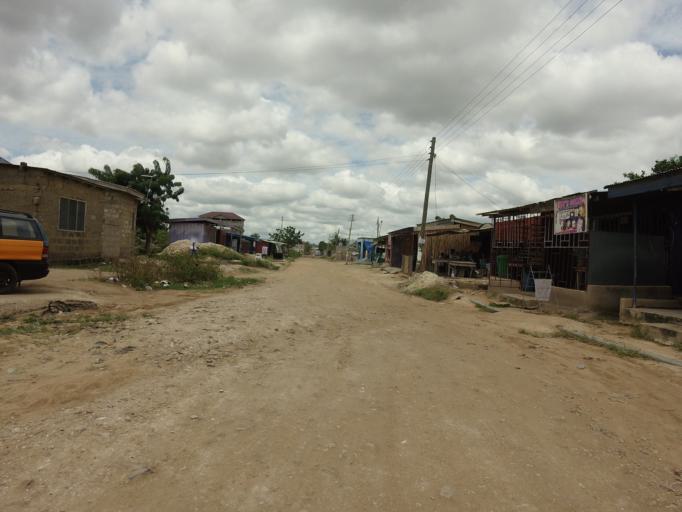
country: GH
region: Central
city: Kasoa
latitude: 5.5503
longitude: -0.3971
